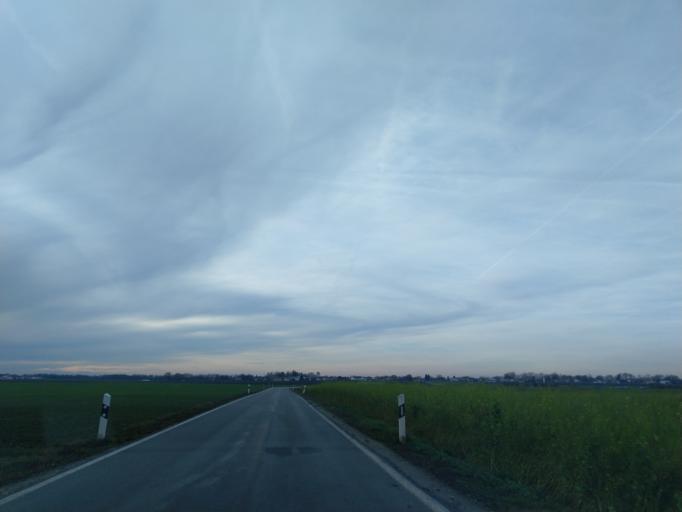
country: DE
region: Bavaria
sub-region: Lower Bavaria
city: Wallerfing
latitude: 48.7087
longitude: 12.8610
